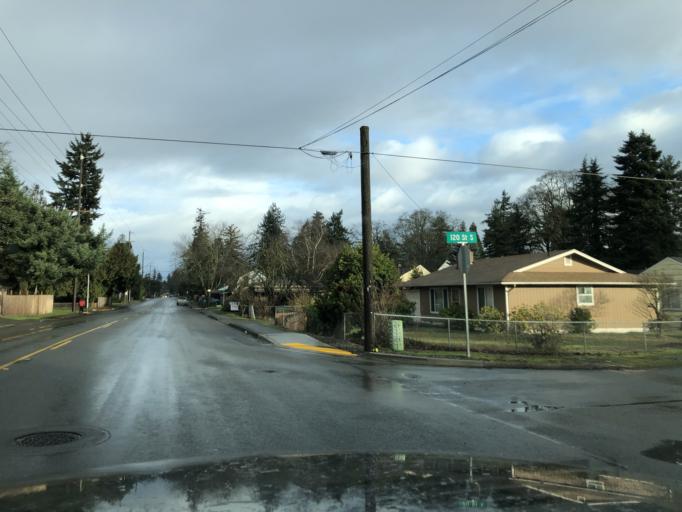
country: US
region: Washington
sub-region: Pierce County
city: Parkland
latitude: 47.1482
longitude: -122.4370
